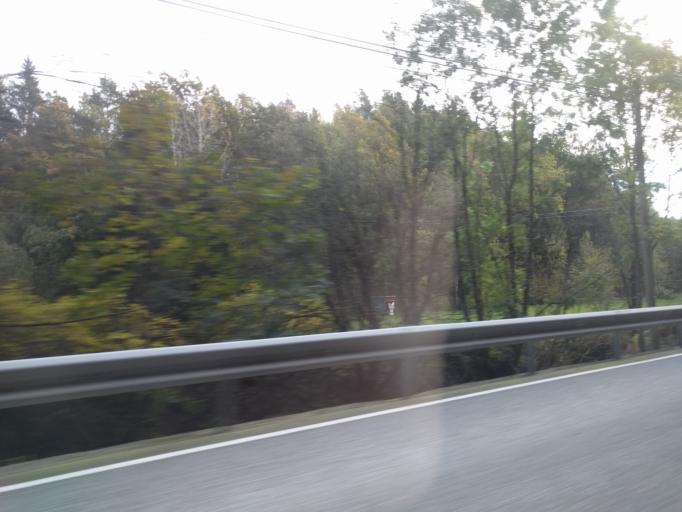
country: NO
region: Vest-Agder
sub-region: Kristiansand
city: Strai
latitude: 58.2411
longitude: 7.8814
